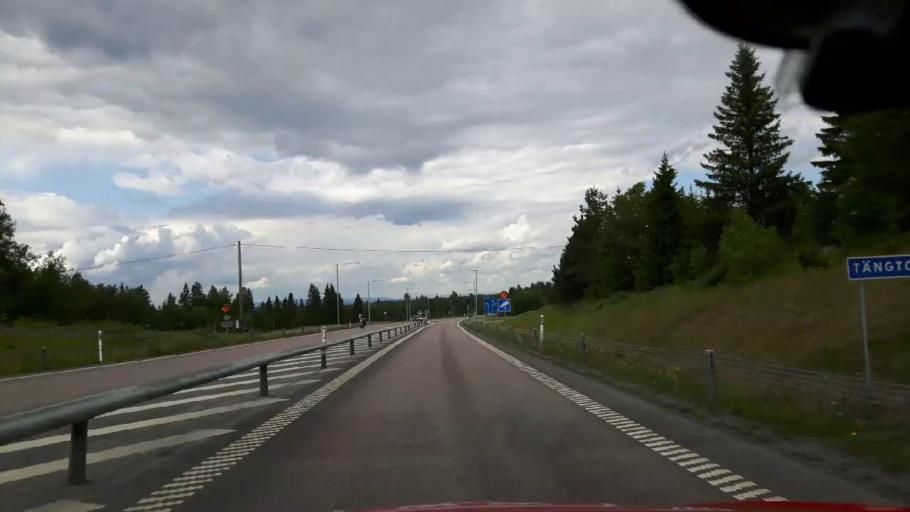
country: SE
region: Jaemtland
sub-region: Krokoms Kommun
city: Krokom
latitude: 63.2658
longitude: 14.5413
